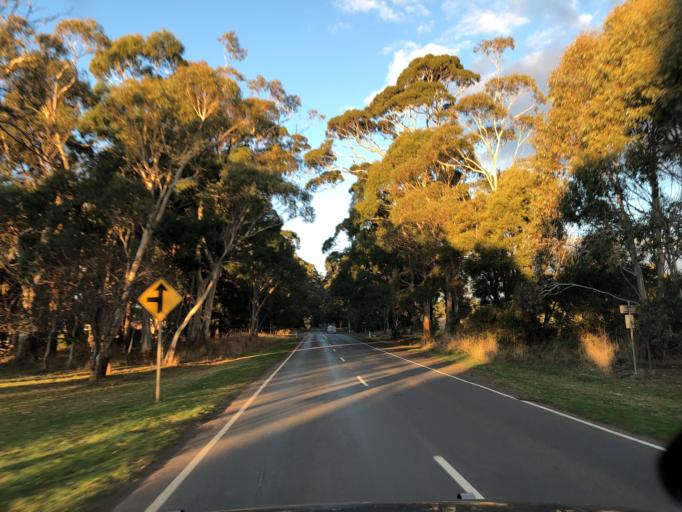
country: AU
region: Victoria
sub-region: Moorabool
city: Bacchus Marsh
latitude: -37.3876
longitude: 144.3318
